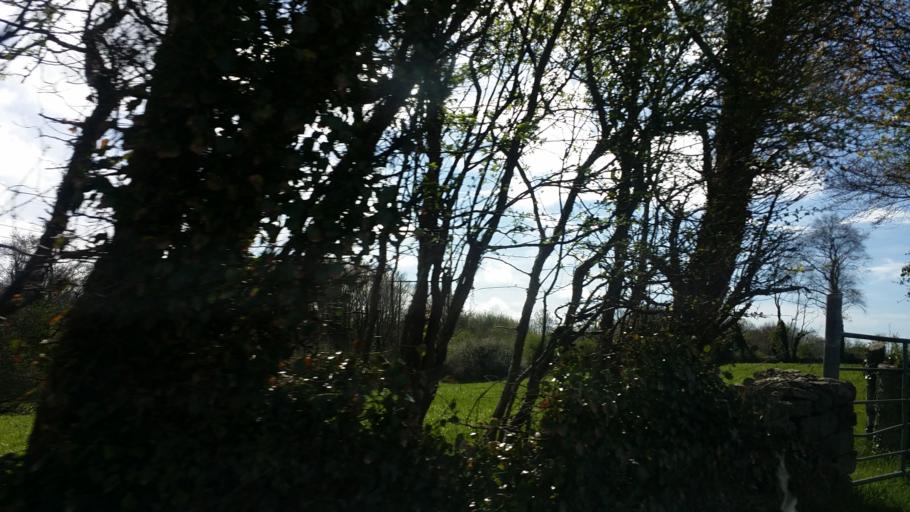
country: IE
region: Ulster
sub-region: County Donegal
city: Ballyshannon
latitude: 54.4852
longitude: -8.1283
